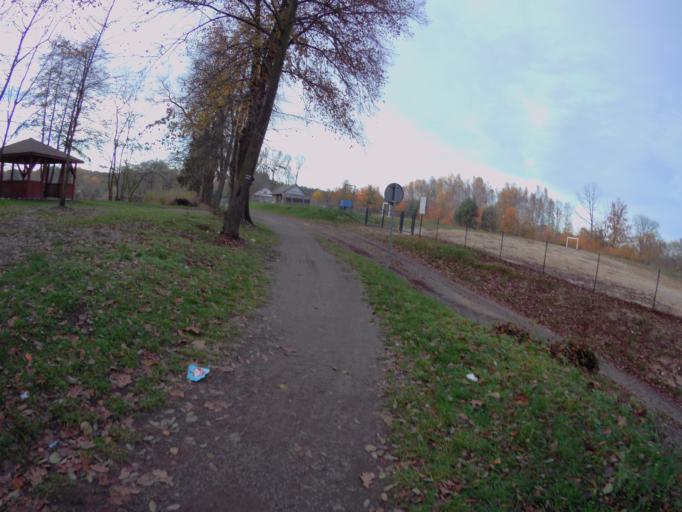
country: PL
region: Subcarpathian Voivodeship
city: Nowa Sarzyna
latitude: 50.3143
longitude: 22.3367
